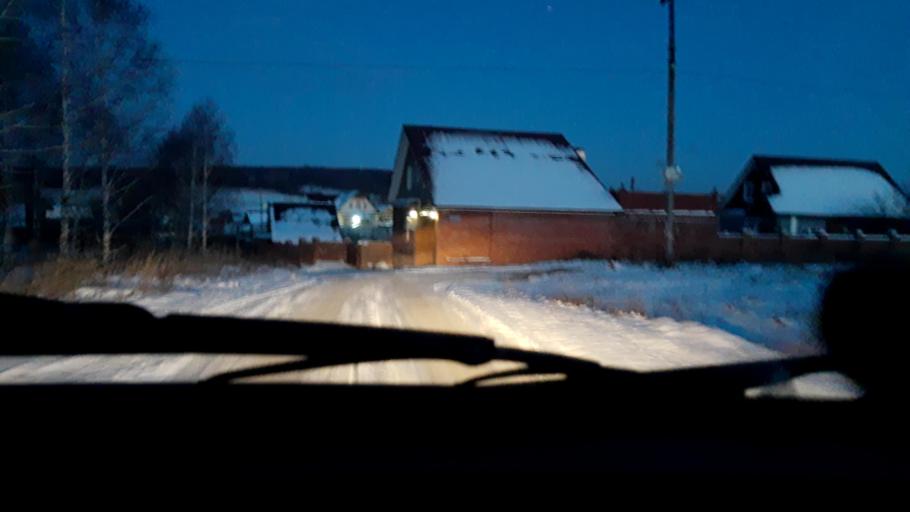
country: RU
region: Bashkortostan
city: Iglino
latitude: 54.7529
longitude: 56.4023
